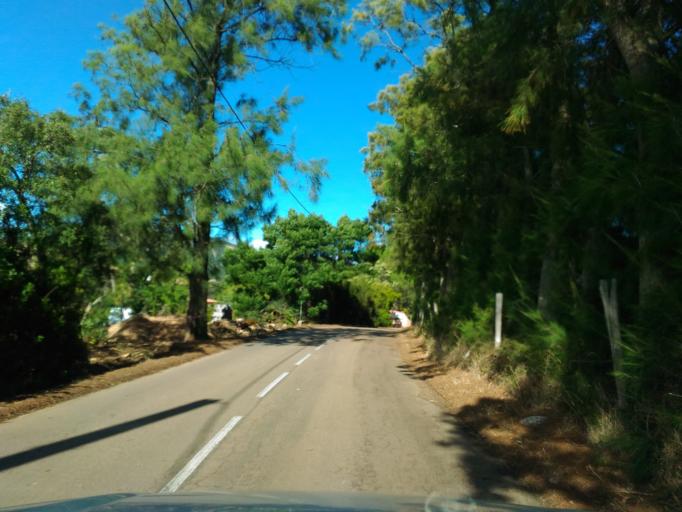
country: FR
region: Corsica
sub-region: Departement de la Corse-du-Sud
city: Porto-Vecchio
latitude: 41.6955
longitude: 9.3706
